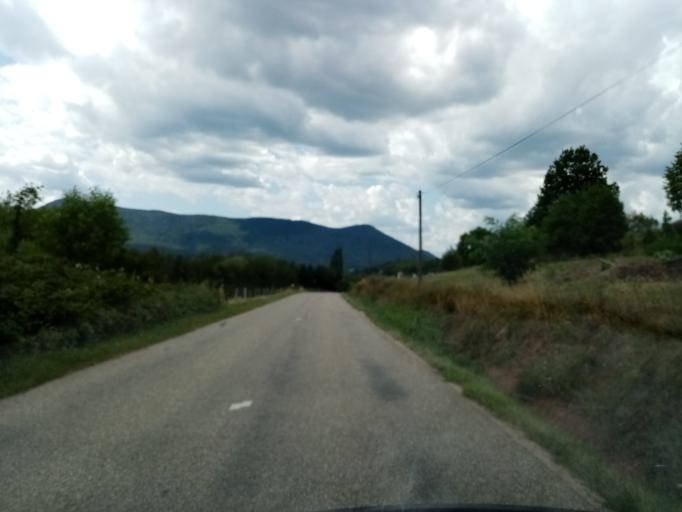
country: FR
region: Alsace
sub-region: Departement du Bas-Rhin
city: Dambach-la-Ville
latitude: 48.3277
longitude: 7.3670
